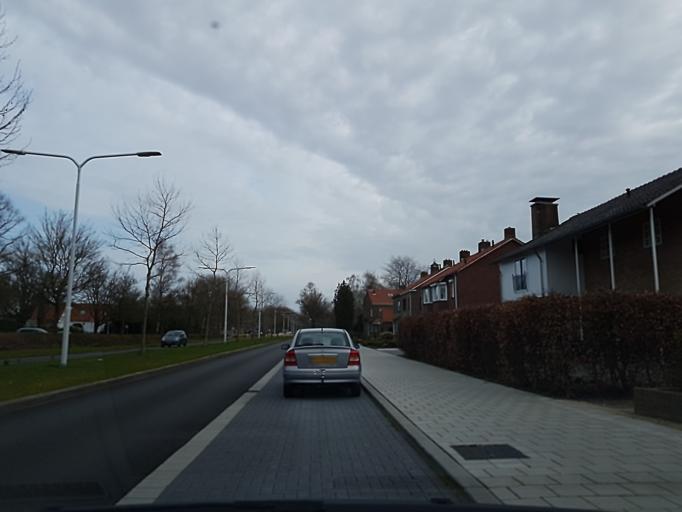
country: NL
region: Zeeland
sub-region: Gemeente Terneuzen
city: Terneuzen
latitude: 51.3312
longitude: 3.8370
